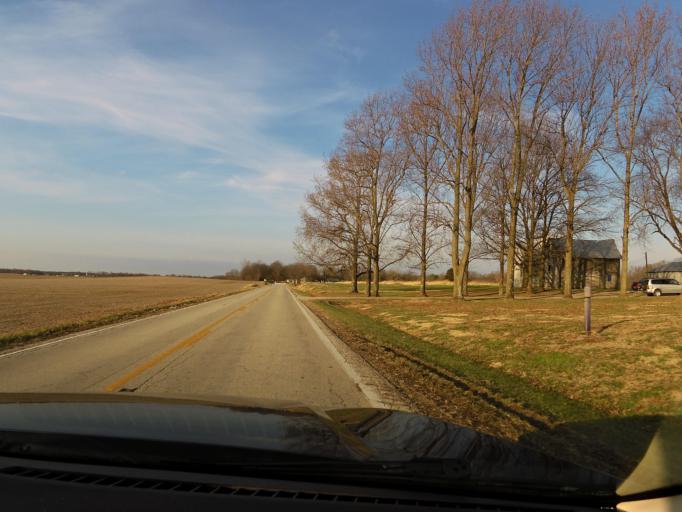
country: US
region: Illinois
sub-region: Fayette County
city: Vandalia
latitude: 38.9220
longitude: -89.2081
